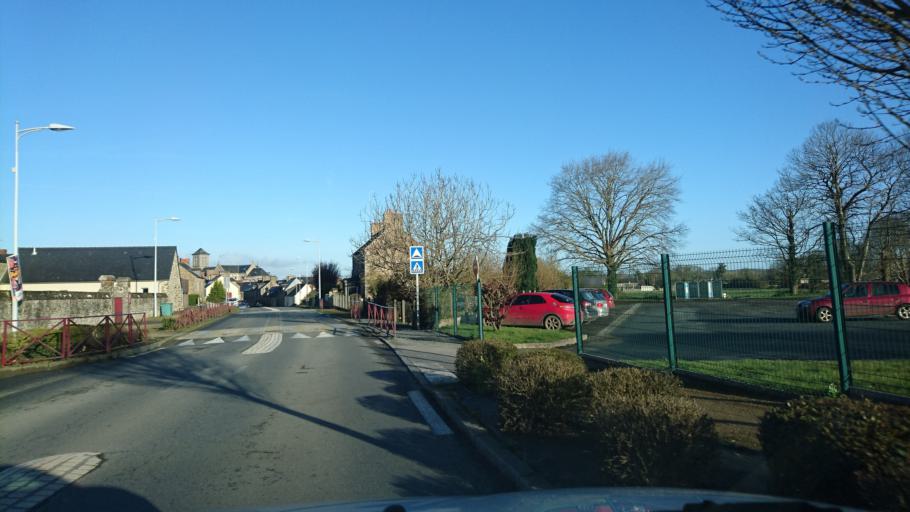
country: FR
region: Brittany
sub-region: Departement d'Ille-et-Vilaine
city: La Boussac
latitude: 48.5118
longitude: -1.6568
